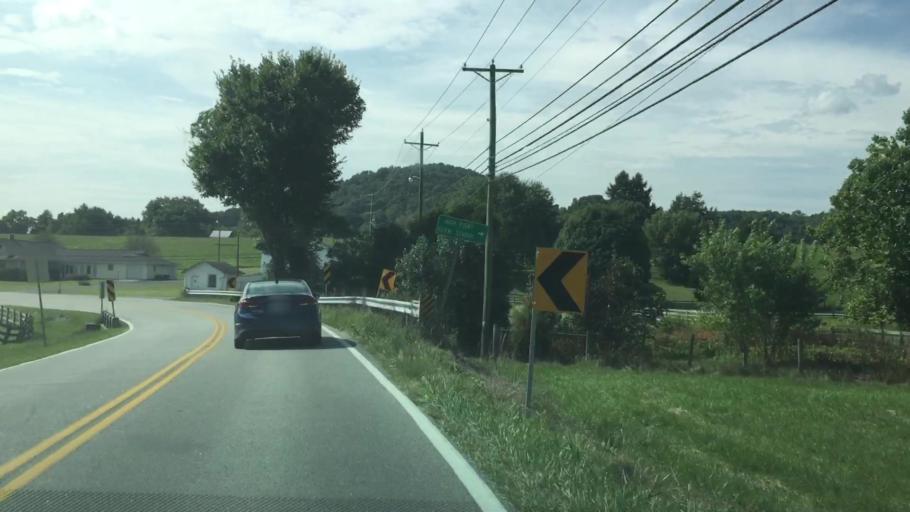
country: US
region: Tennessee
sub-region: Sullivan County
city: Fairmount
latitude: 36.6045
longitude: -82.1199
